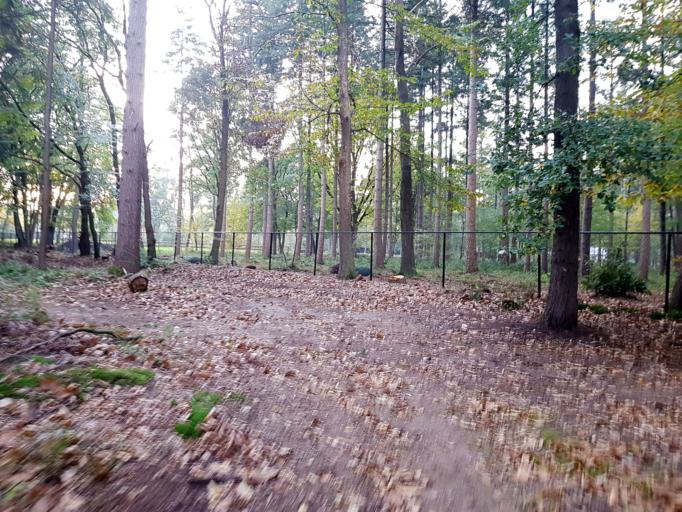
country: NL
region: Utrecht
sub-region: Gemeente Utrechtse Heuvelrug
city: Leersum
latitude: 52.0289
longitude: 5.4066
